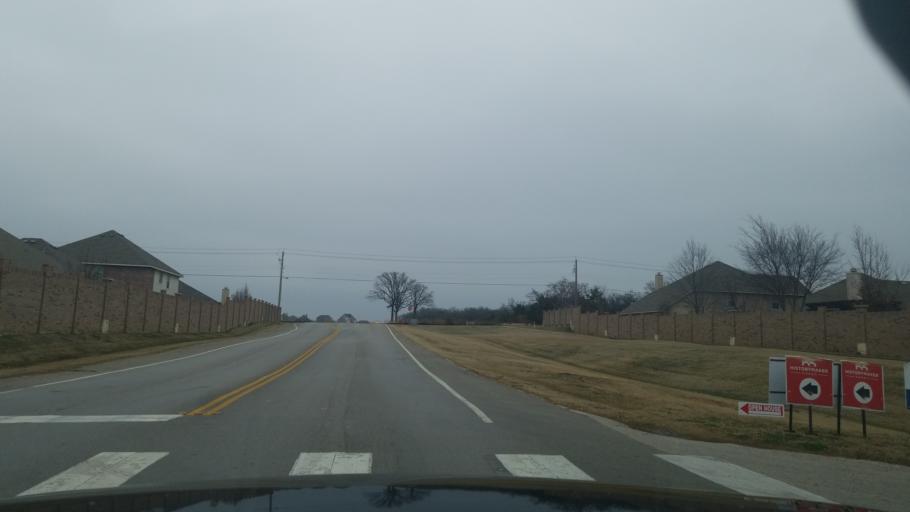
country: US
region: Texas
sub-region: Denton County
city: Corinth
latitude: 33.1695
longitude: -97.0710
